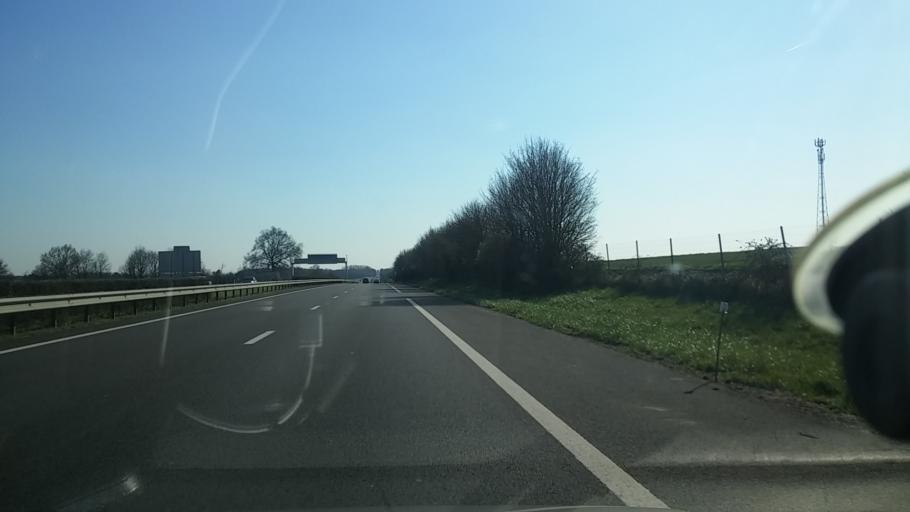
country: FR
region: Centre
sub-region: Departement du Cher
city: Massay
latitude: 47.1880
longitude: 2.0168
